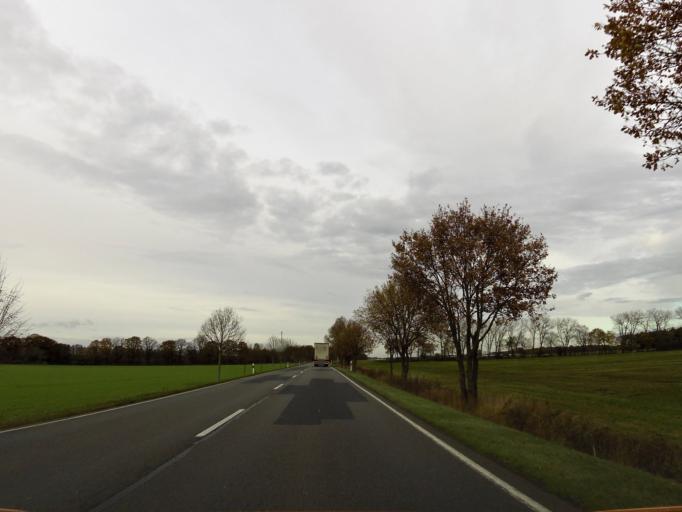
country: DE
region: Saxony-Anhalt
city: Pretzier
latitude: 52.7591
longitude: 11.2390
